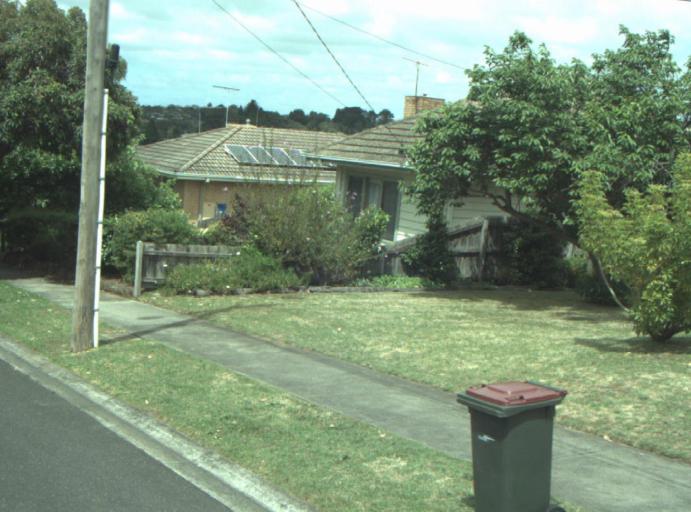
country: AU
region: Victoria
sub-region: Greater Geelong
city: Wandana Heights
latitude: -38.1687
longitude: 144.3212
